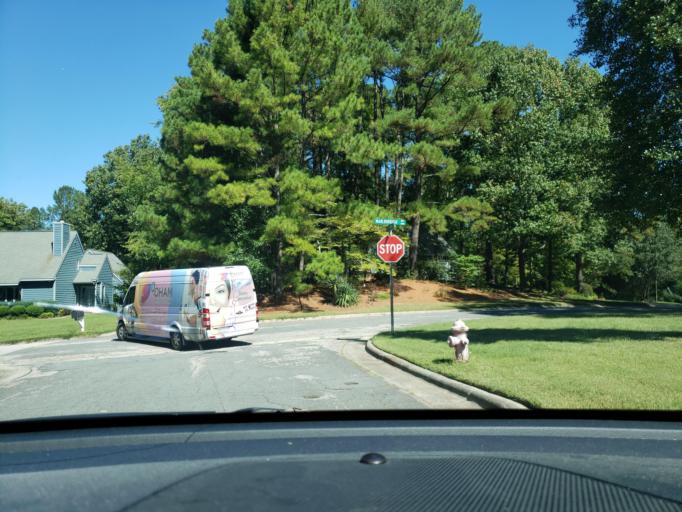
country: US
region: North Carolina
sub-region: Durham County
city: Durham
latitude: 35.9150
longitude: -78.9427
